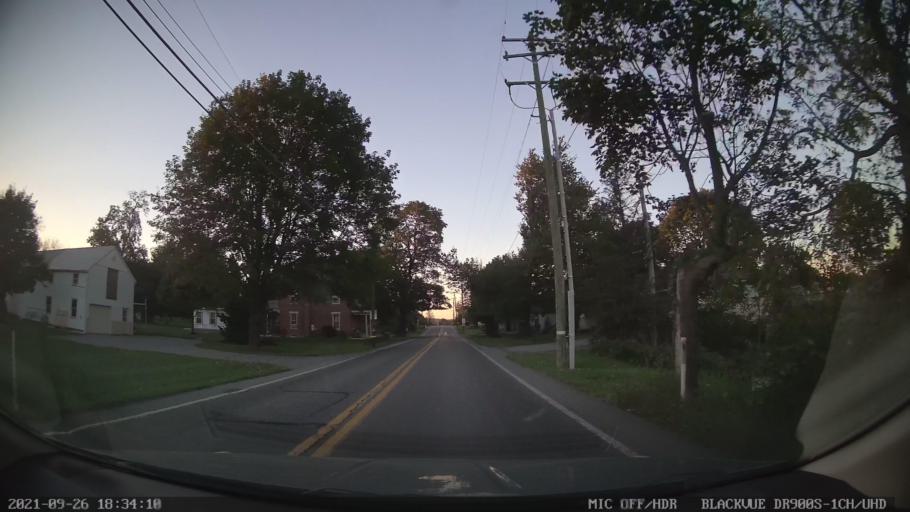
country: US
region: Pennsylvania
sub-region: Berks County
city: Kutztown
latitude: 40.5081
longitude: -75.7708
